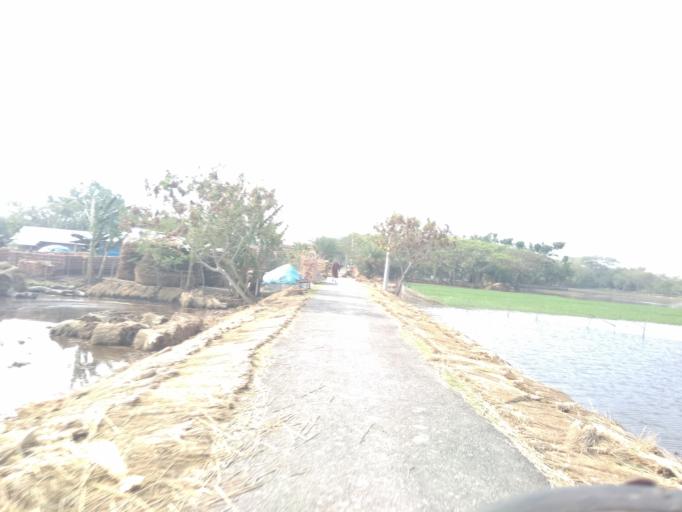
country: IN
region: West Bengal
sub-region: North 24 Parganas
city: Gosaba
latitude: 22.2584
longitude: 89.1152
